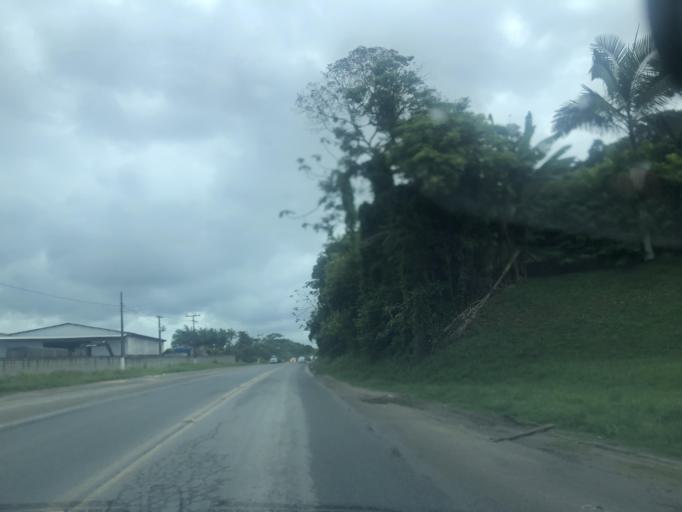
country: BR
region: Santa Catarina
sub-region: Sao Francisco Do Sul
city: Sao Francisco do Sul
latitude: -26.2411
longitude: -48.6176
